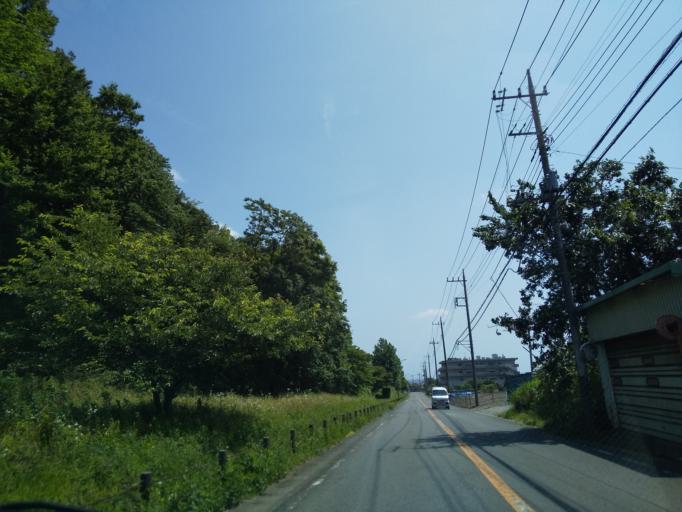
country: JP
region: Kanagawa
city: Zama
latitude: 35.5134
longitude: 139.3915
